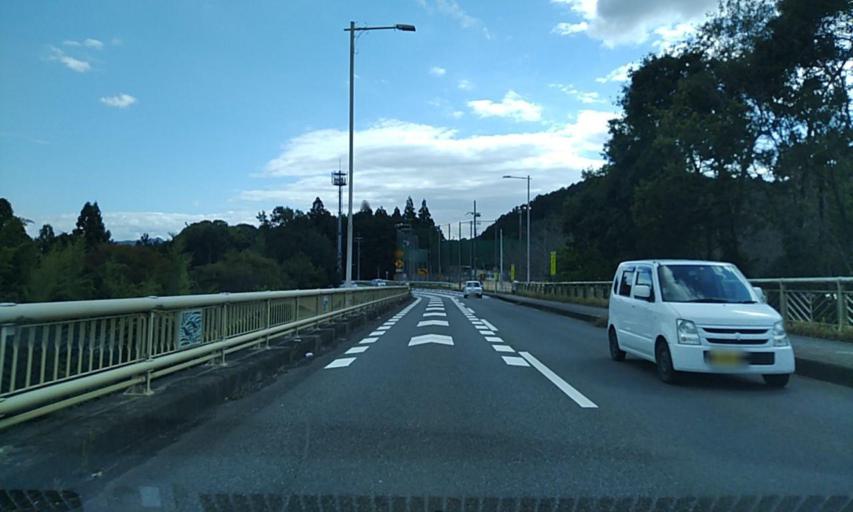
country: JP
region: Kyoto
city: Fukuchiyama
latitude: 35.3026
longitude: 135.1440
